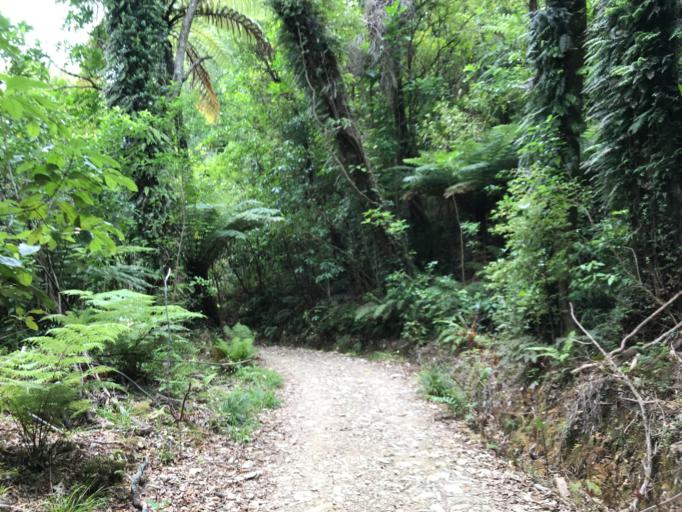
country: NZ
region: Marlborough
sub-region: Marlborough District
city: Picton
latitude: -41.0951
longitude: 174.1884
